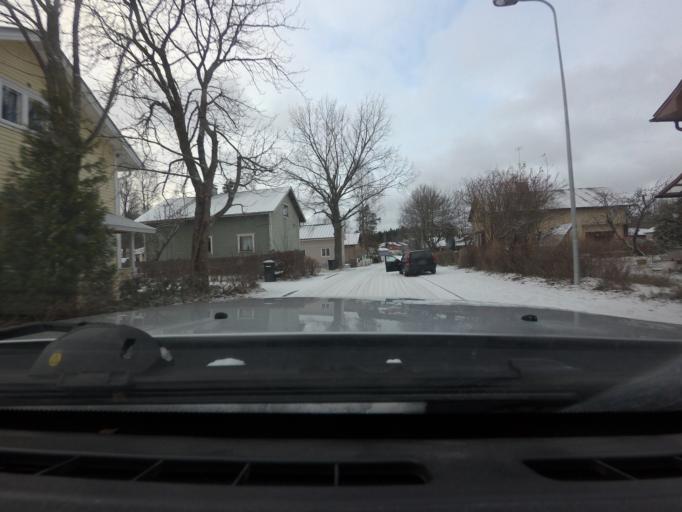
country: FI
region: Uusimaa
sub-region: Helsinki
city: Kilo
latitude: 60.2122
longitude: 24.7879
